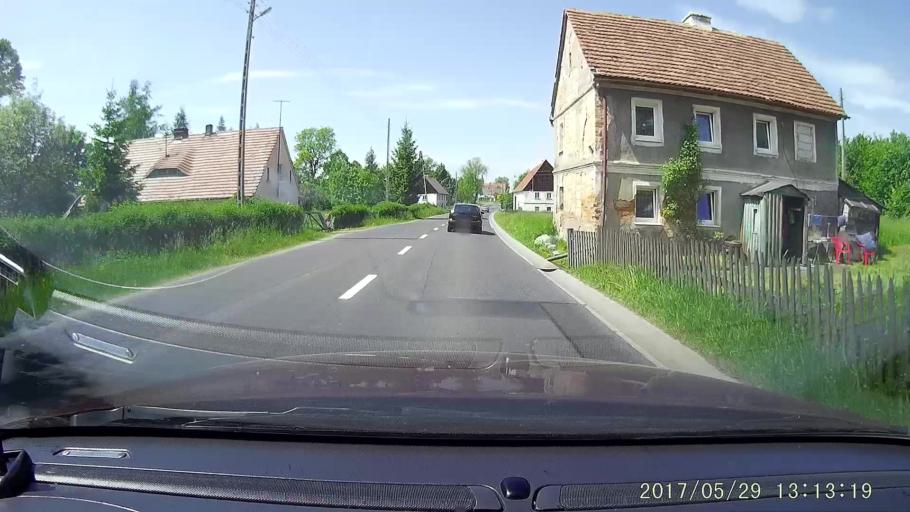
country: PL
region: Lower Silesian Voivodeship
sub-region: Powiat lwowecki
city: Lubomierz
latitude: 50.9739
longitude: 15.4998
